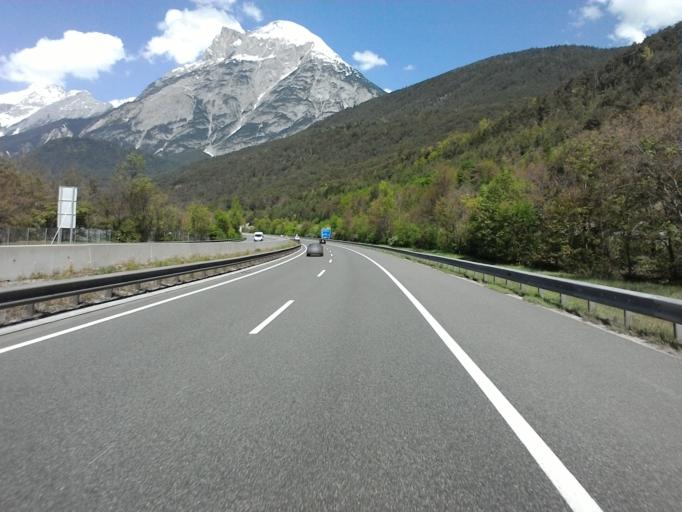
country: AT
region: Tyrol
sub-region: Politischer Bezirk Innsbruck Land
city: Pettnau
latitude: 47.3068
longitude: 11.1213
